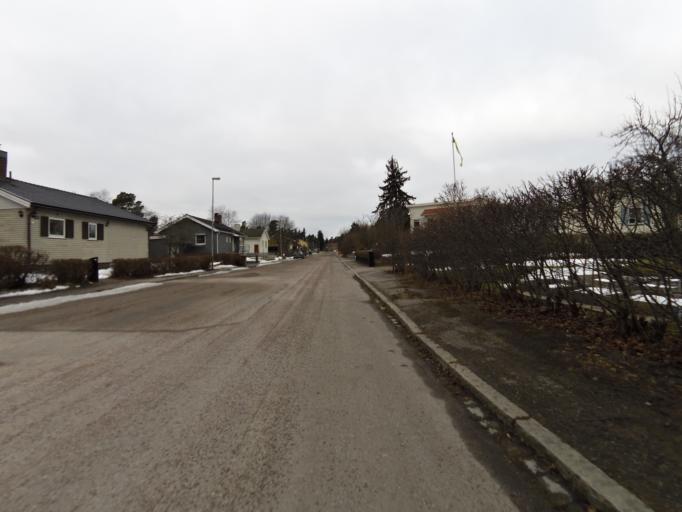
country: SE
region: Gaevleborg
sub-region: Gavle Kommun
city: Gavle
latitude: 60.6584
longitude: 17.1400
